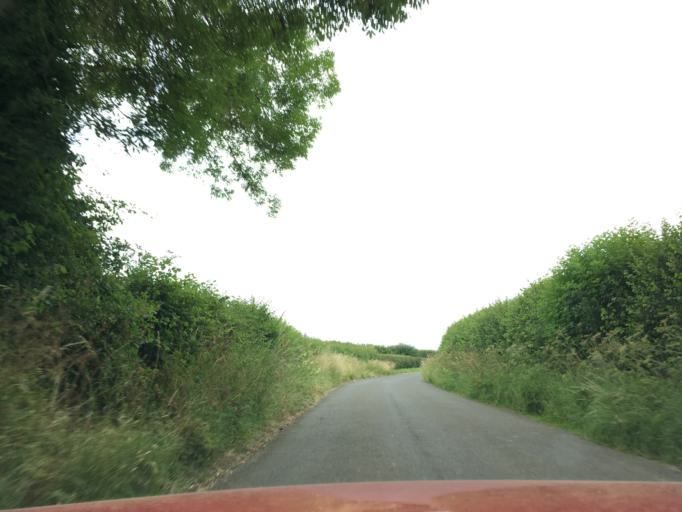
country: GB
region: England
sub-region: Oxfordshire
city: Bloxham
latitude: 51.9695
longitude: -1.3812
